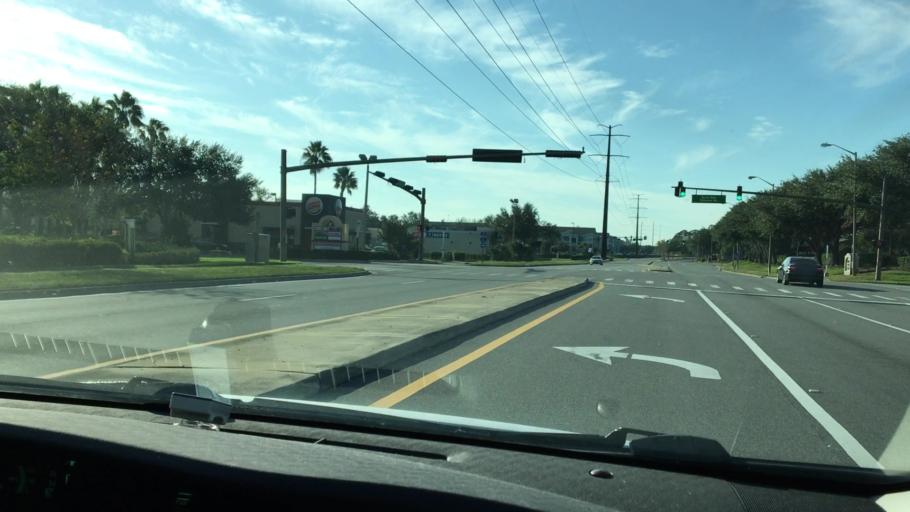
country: US
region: Florida
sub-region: Seminole County
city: Lake Mary
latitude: 28.8082
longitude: -81.3351
